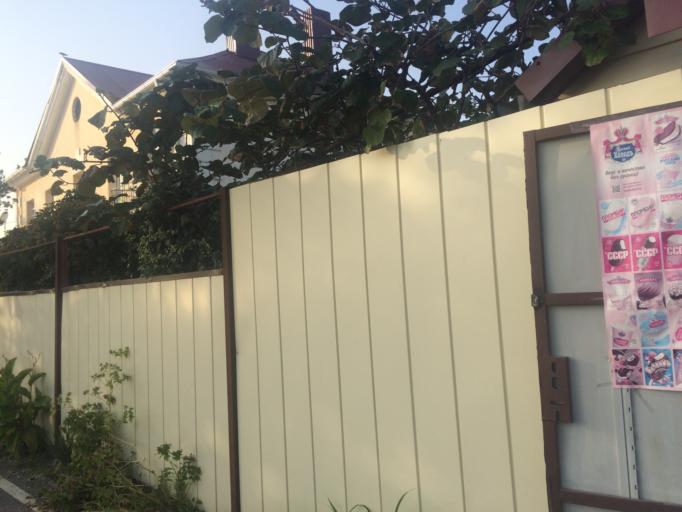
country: RU
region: Krasnodarskiy
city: Adler
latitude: 43.3871
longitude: 39.9888
